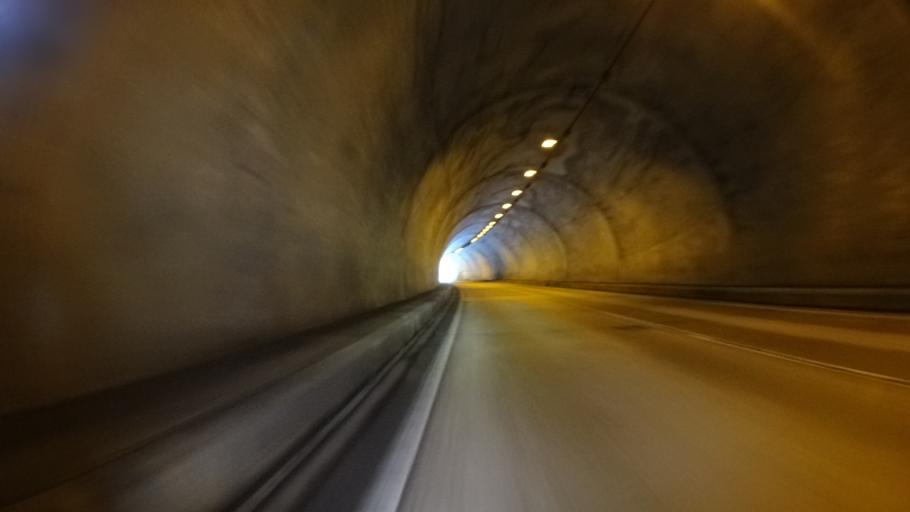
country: JP
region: Gunma
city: Tomioka
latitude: 36.0846
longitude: 138.7391
